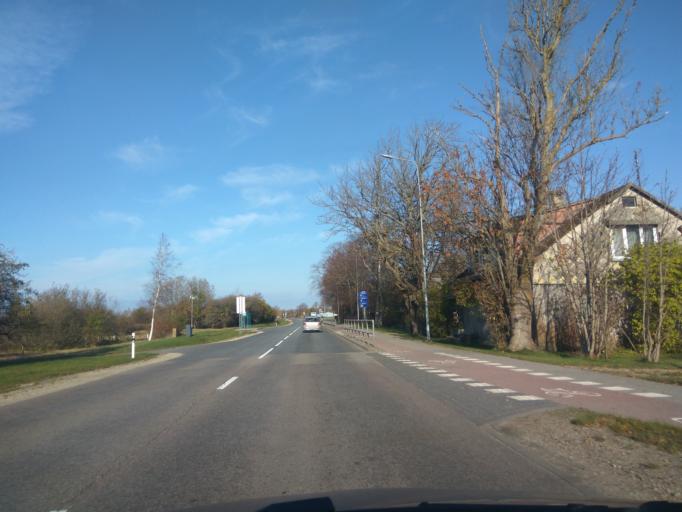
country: LV
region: Ventspils
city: Ventspils
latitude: 57.3650
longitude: 21.5636
